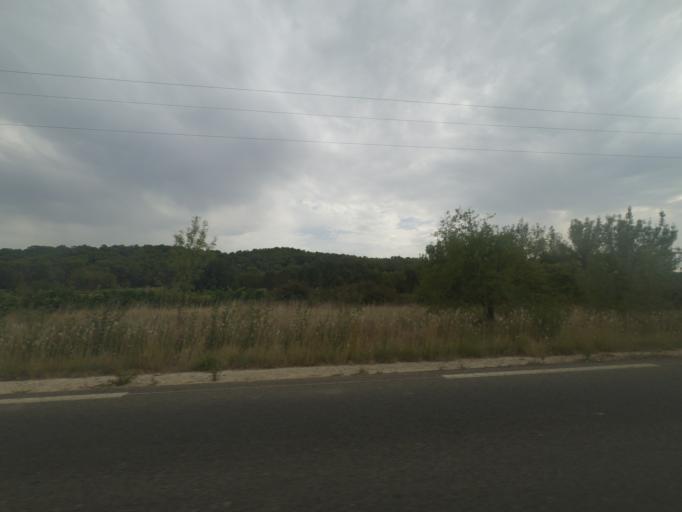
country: FR
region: Languedoc-Roussillon
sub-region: Departement de l'Herault
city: Les Matelles
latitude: 43.7379
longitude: 3.8333
